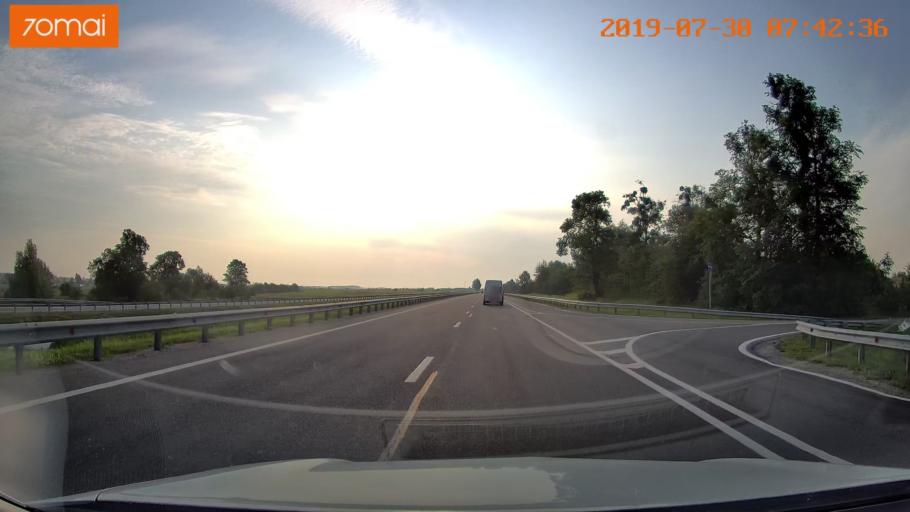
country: RU
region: Kaliningrad
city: Gvardeysk
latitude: 54.6480
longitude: 21.2836
